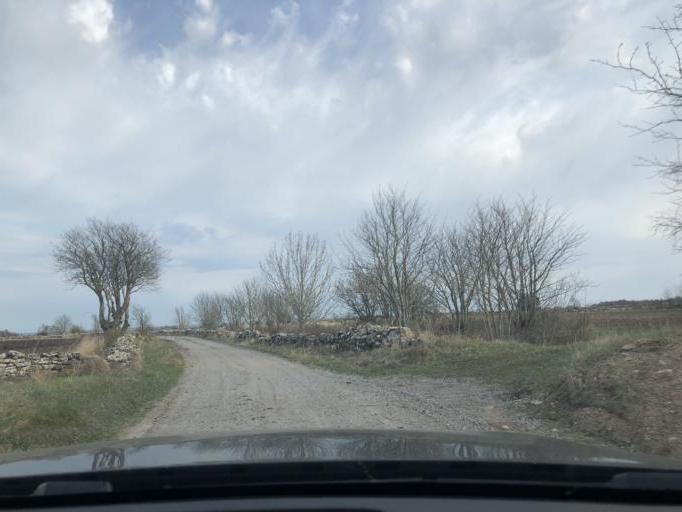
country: SE
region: Kalmar
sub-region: Morbylanga Kommun
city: Sodra Sandby
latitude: 56.5588
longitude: 16.6210
